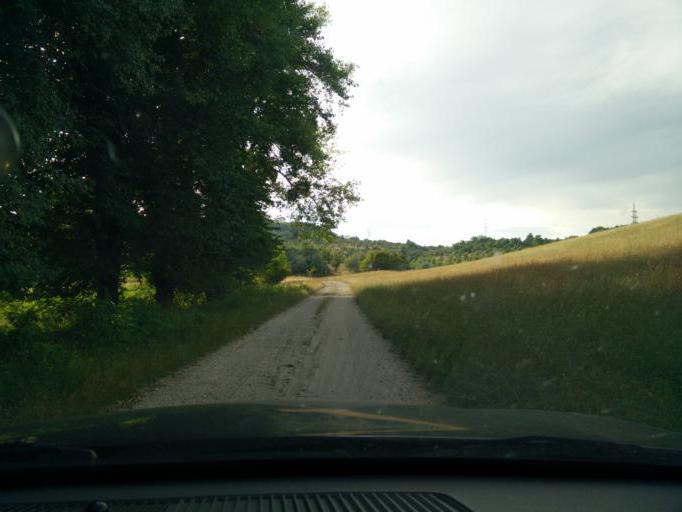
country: HU
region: Fejer
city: Szarliget
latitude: 47.5156
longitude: 18.4671
